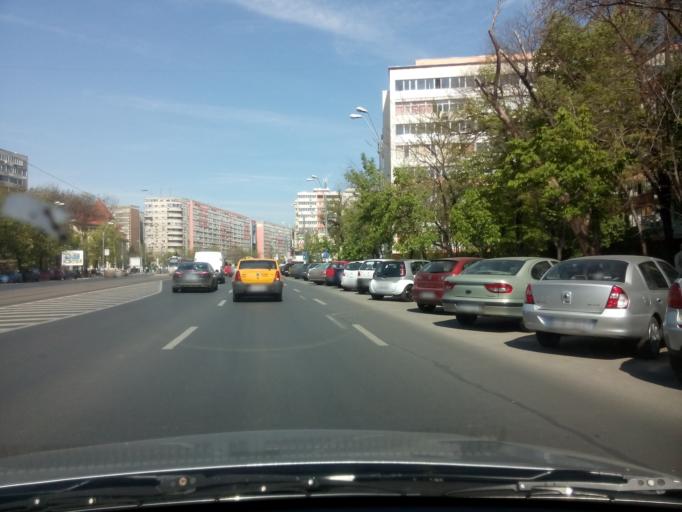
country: RO
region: Bucuresti
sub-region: Municipiul Bucuresti
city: Bucharest
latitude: 44.4429
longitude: 26.1309
